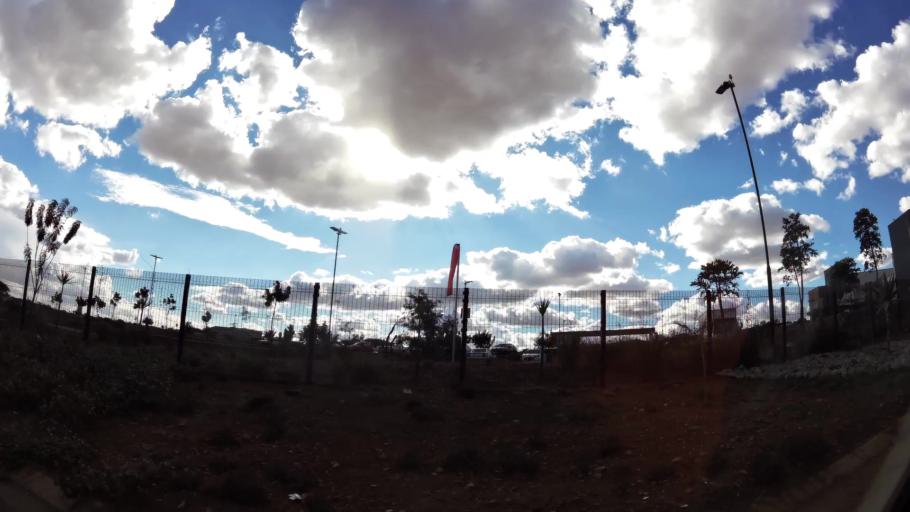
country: ZA
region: Limpopo
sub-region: Capricorn District Municipality
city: Polokwane
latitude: -23.9029
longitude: 29.4926
